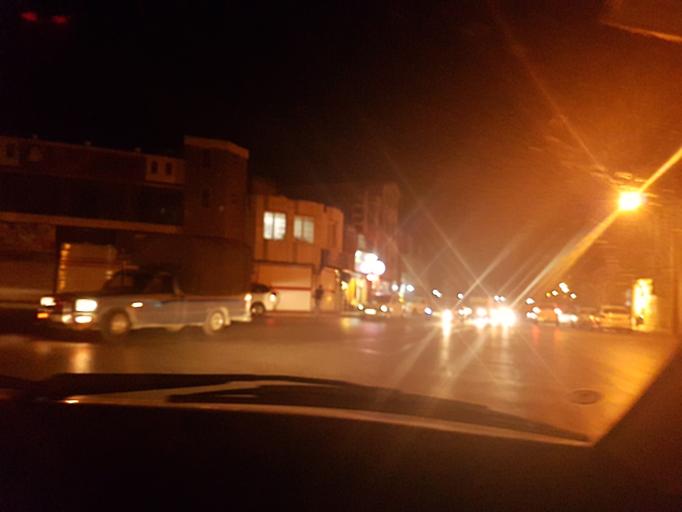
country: IR
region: Markazi
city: Arak
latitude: 34.0737
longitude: 49.6753
